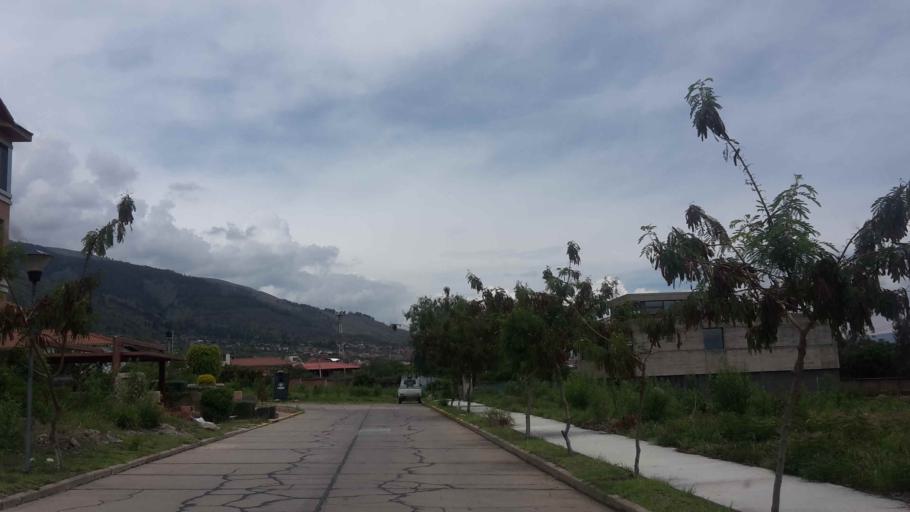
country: BO
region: Cochabamba
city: Cochabamba
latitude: -17.3425
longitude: -66.1847
